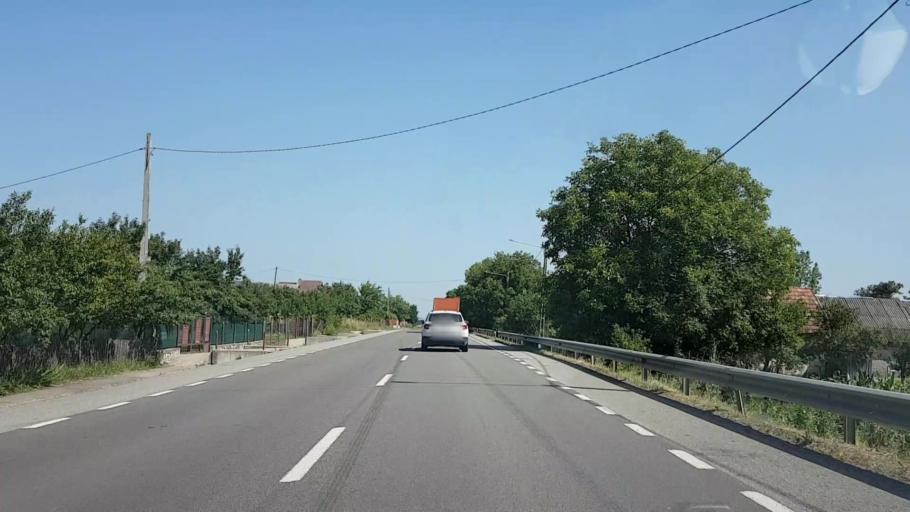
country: RO
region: Bistrita-Nasaud
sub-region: Comuna Sieu-Odorhei
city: Sieu-Odorhei
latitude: 47.1291
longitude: 24.3143
